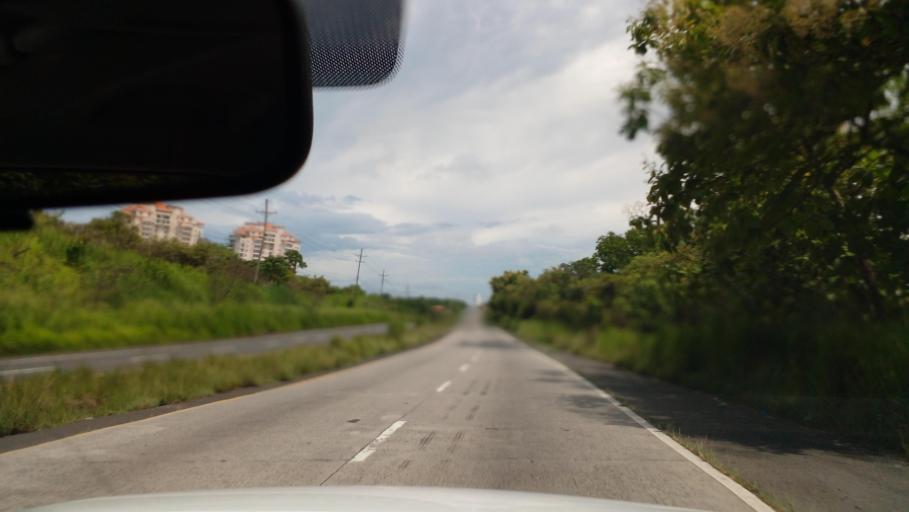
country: PA
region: Panama
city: Nueva Gorgona
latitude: 8.4984
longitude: -79.9582
